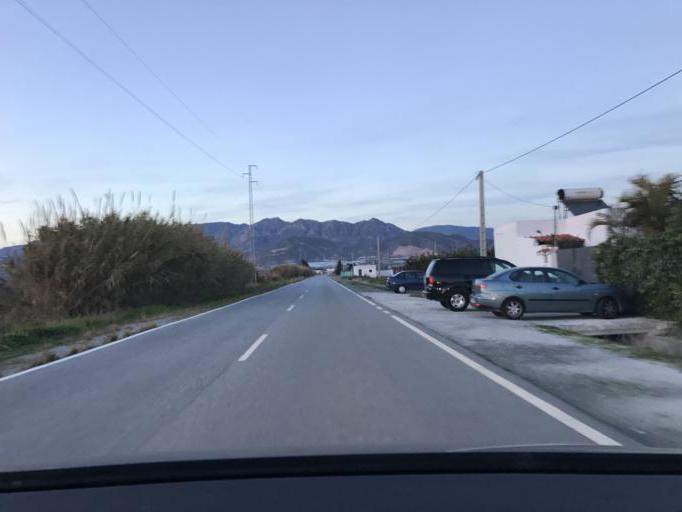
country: ES
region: Andalusia
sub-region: Provincia de Granada
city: Salobrena
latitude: 36.7370
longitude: -3.5630
